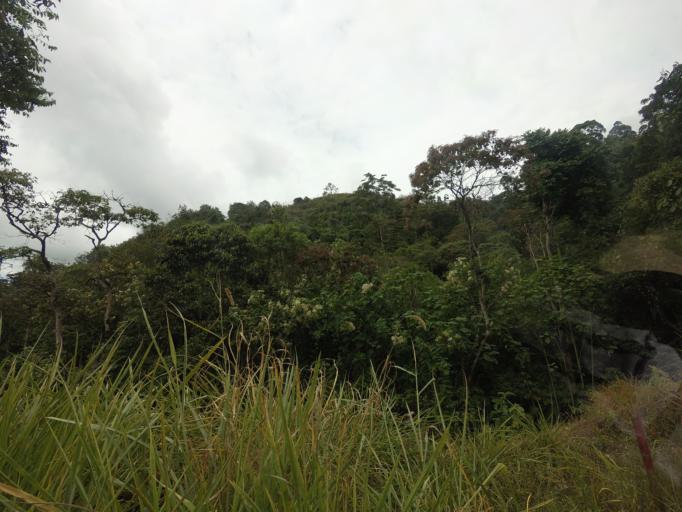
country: CO
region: Huila
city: San Agustin
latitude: 1.9282
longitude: -76.3003
